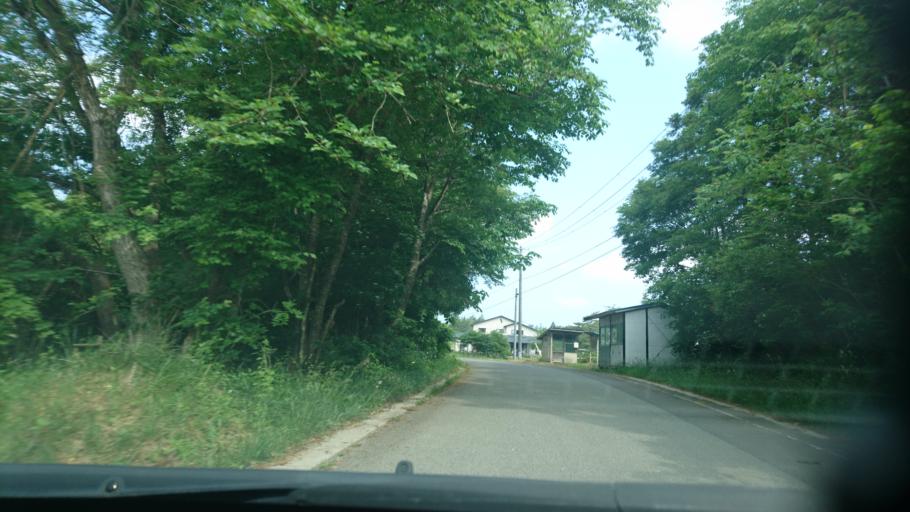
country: JP
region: Iwate
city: Ichinoseki
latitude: 38.9019
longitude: 141.2405
